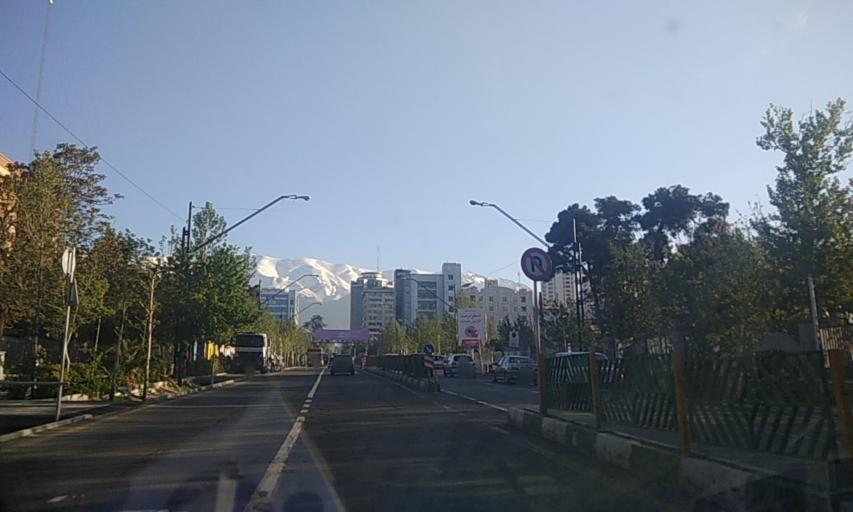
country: IR
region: Tehran
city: Tajrish
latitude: 35.7644
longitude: 51.4104
